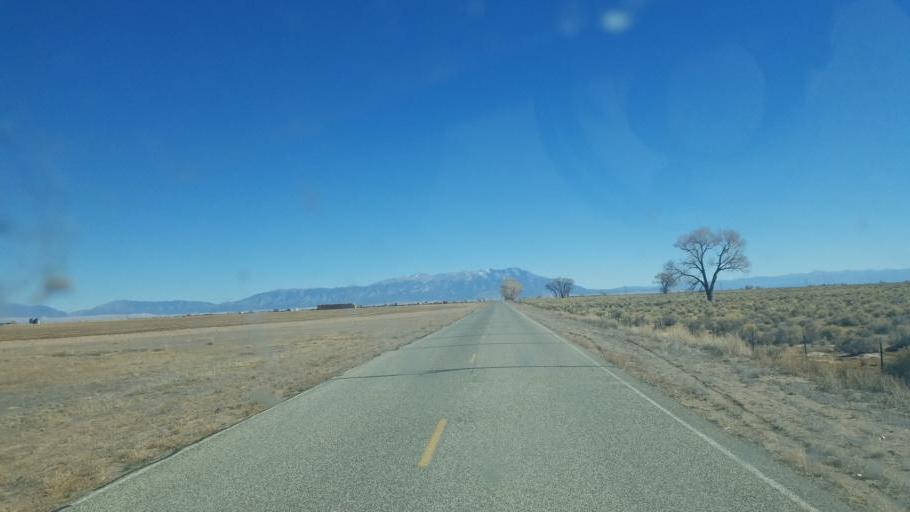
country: US
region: Colorado
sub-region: Alamosa County
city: Alamosa
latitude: 37.5743
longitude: -105.9738
